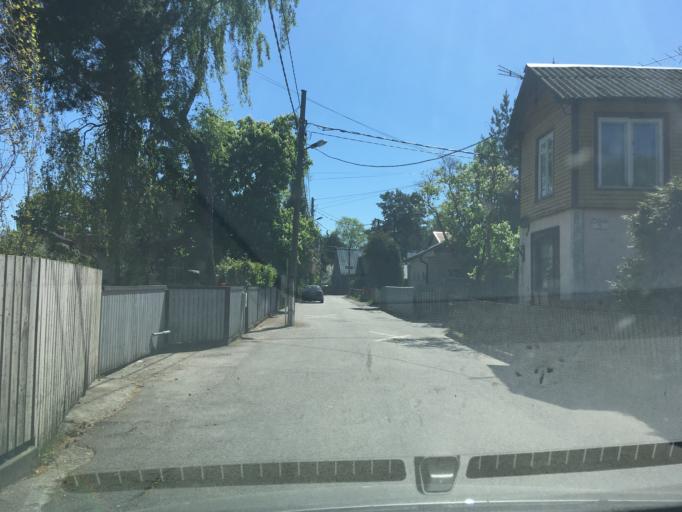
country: EE
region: Harju
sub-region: Saue vald
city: Laagri
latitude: 59.3874
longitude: 24.6735
